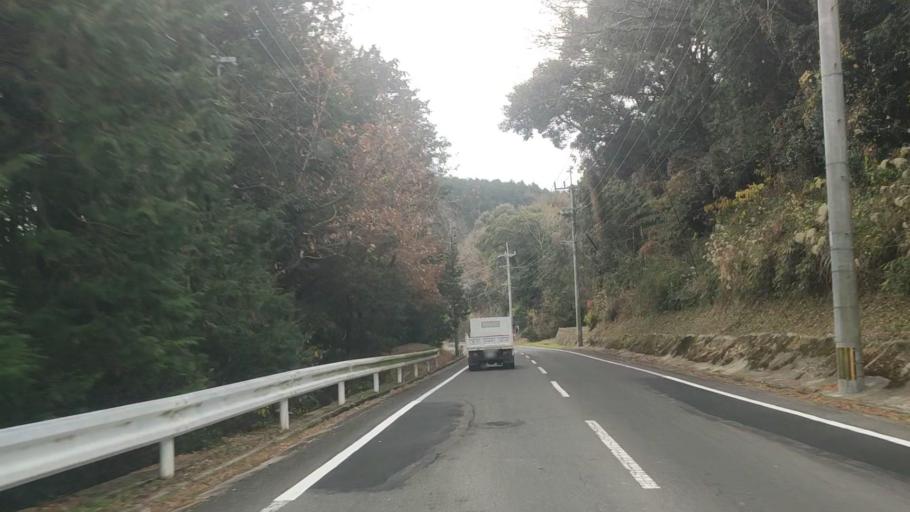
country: JP
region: Nagasaki
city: Shimabara
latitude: 32.8514
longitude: 130.2754
